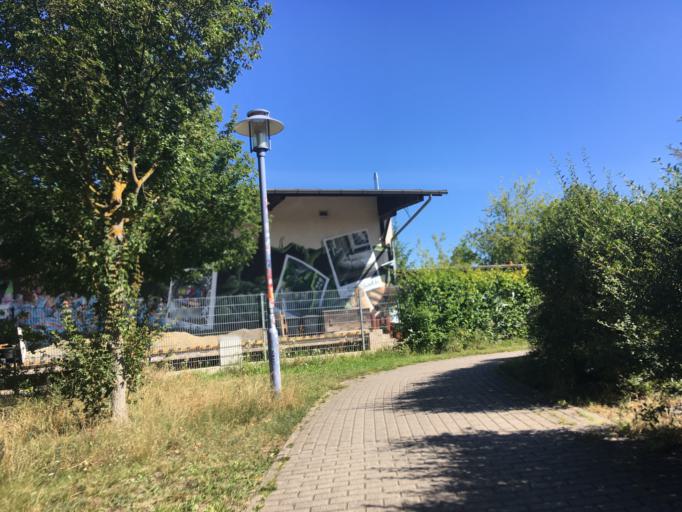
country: DE
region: Brandenburg
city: Petershagen
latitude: 52.5253
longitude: 13.7607
